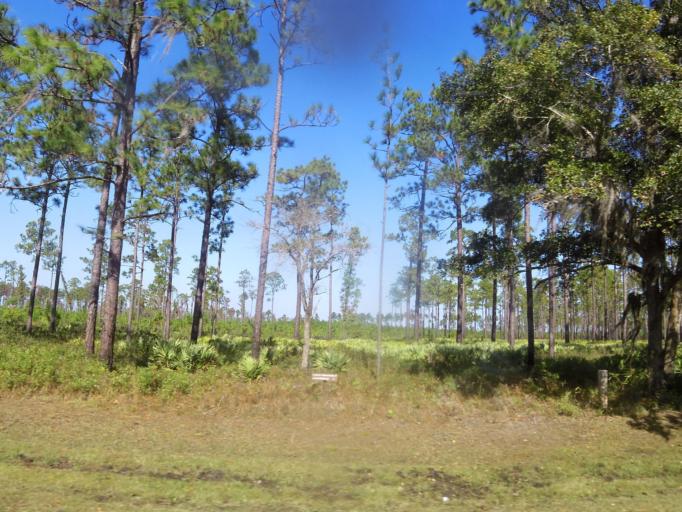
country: US
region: Georgia
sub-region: Charlton County
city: Folkston
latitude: 30.7397
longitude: -82.1386
